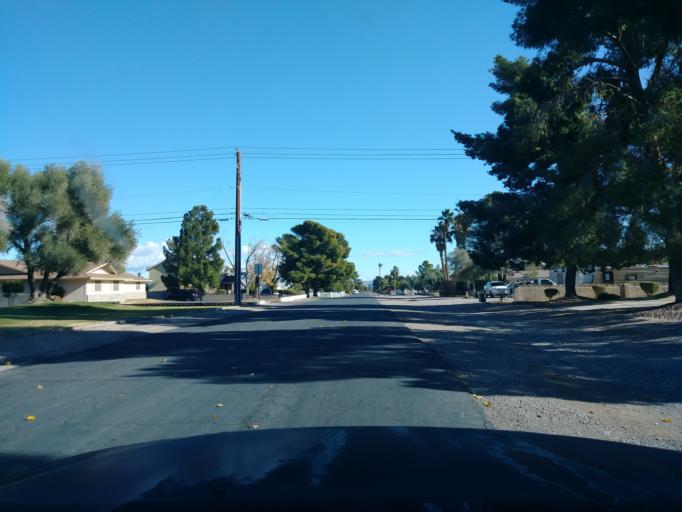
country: US
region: Nevada
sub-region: Clark County
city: Spring Valley
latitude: 36.1481
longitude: -115.2183
